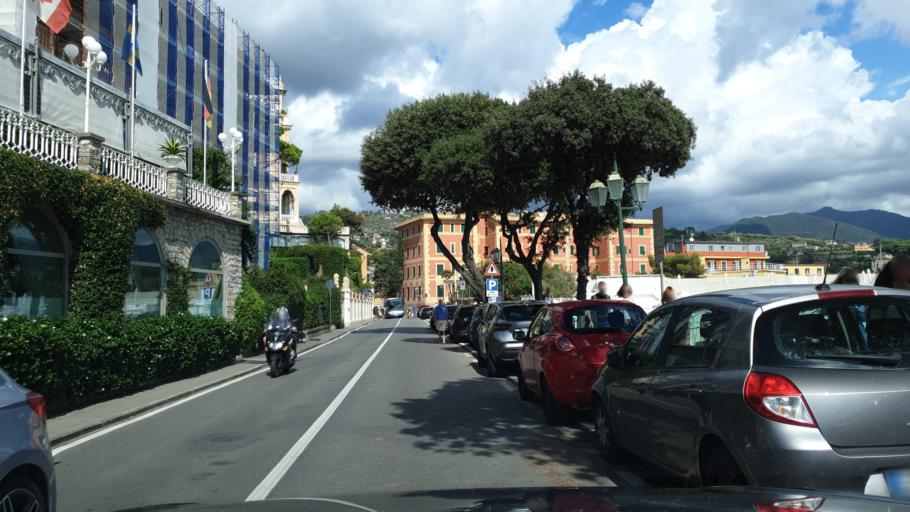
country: IT
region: Liguria
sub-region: Provincia di Genova
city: Santa Margherita Ligure
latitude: 44.3279
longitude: 9.2152
